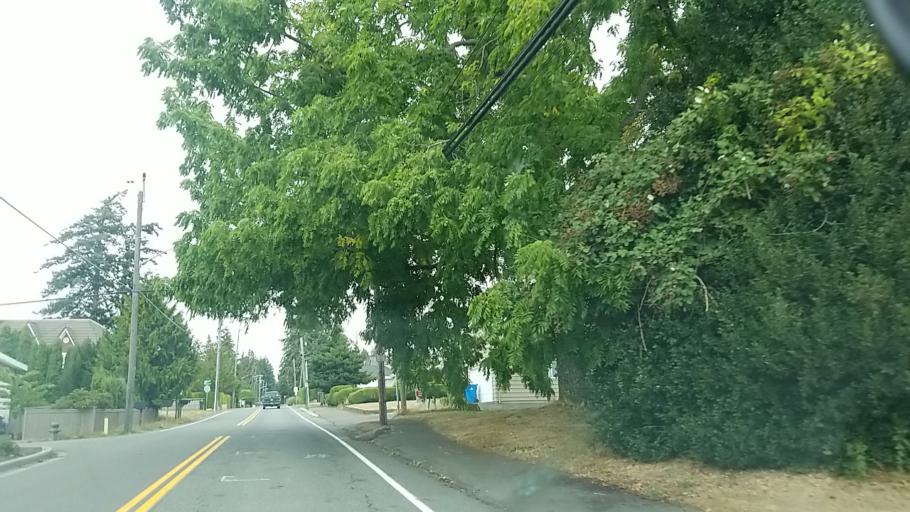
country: US
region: Washington
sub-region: Snohomish County
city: Woodway
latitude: 47.7736
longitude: -122.3828
